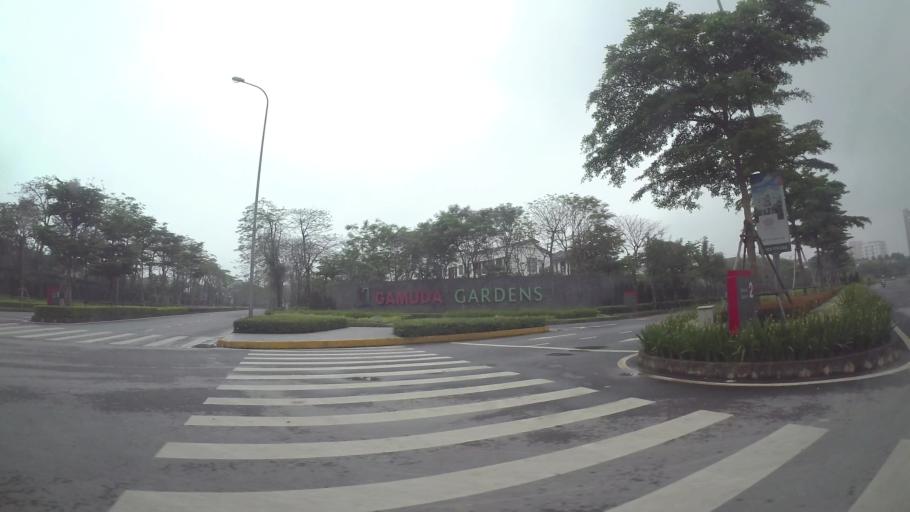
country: VN
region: Ha Noi
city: Van Dien
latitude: 20.9729
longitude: 105.8782
